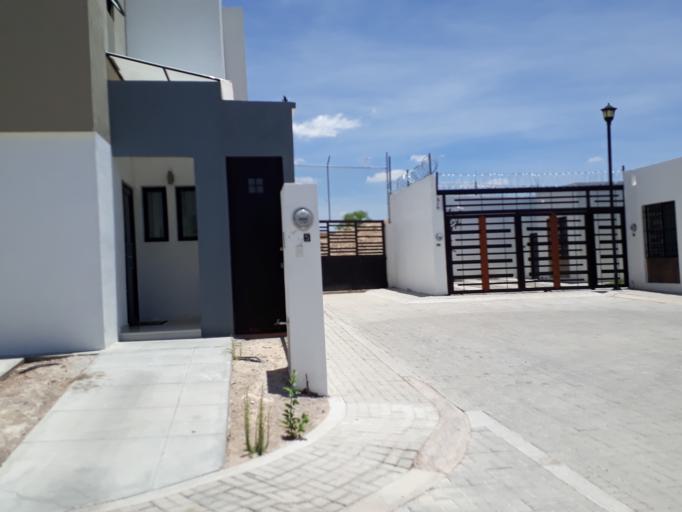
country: MX
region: Aguascalientes
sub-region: Aguascalientes
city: San Sebastian [Fraccionamiento]
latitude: 21.8059
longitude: -102.3030
